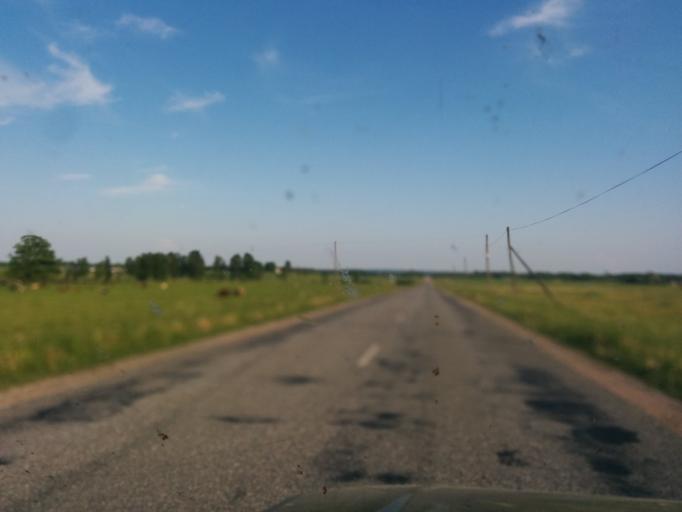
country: LV
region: Talsu Rajons
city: Valdemarpils
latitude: 57.3413
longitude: 22.5058
